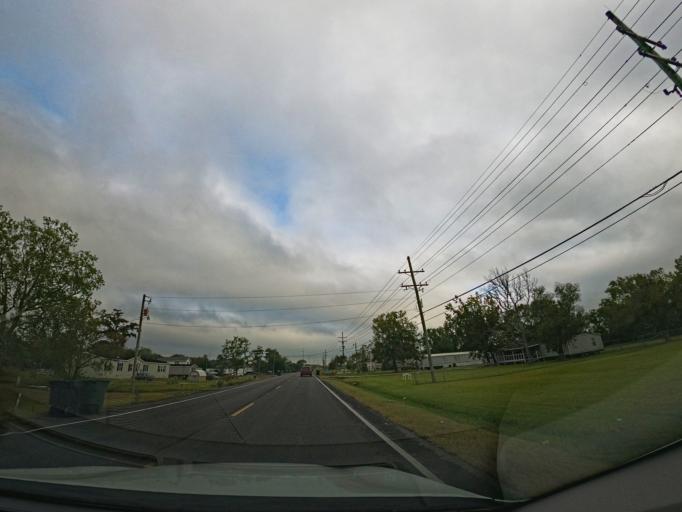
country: US
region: Louisiana
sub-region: Terrebonne Parish
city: Presquille
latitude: 29.5155
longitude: -90.6756
